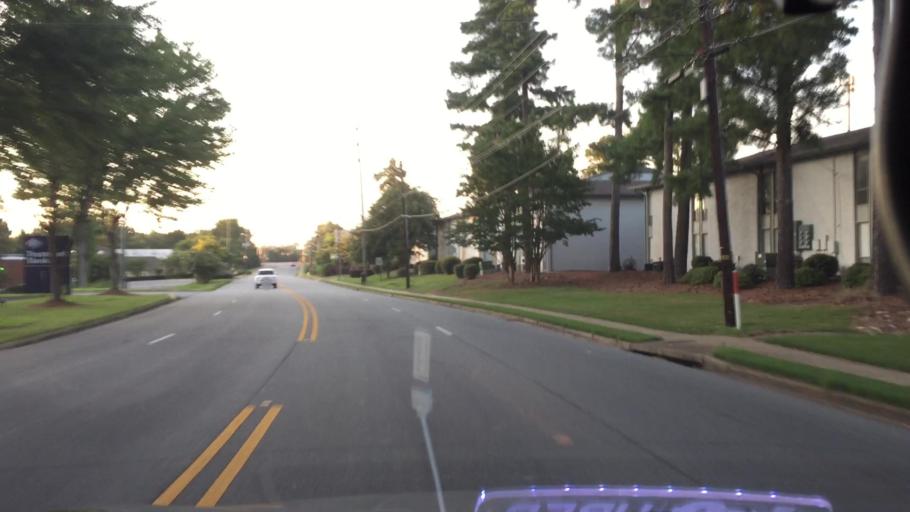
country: US
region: Alabama
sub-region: Lee County
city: Auburn
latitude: 32.6125
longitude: -85.4645
